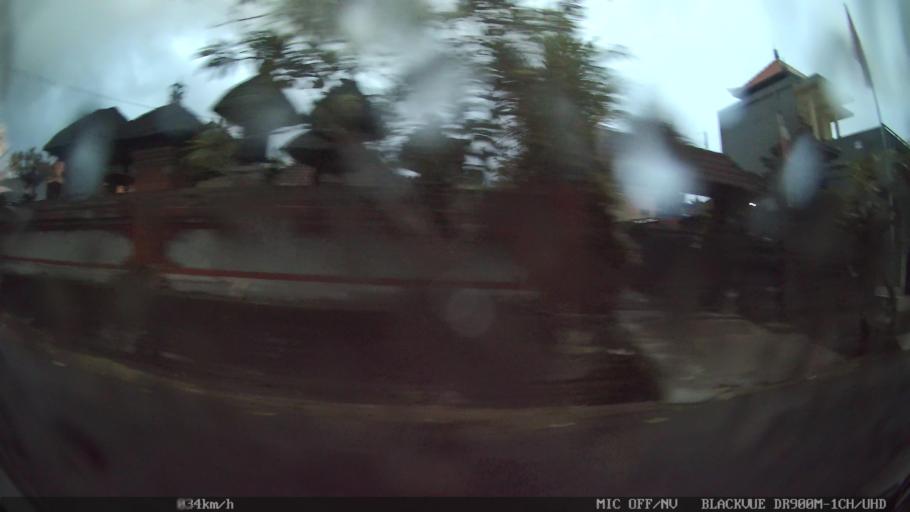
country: ID
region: Bali
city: Banjar Batur
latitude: -8.6049
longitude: 115.2210
